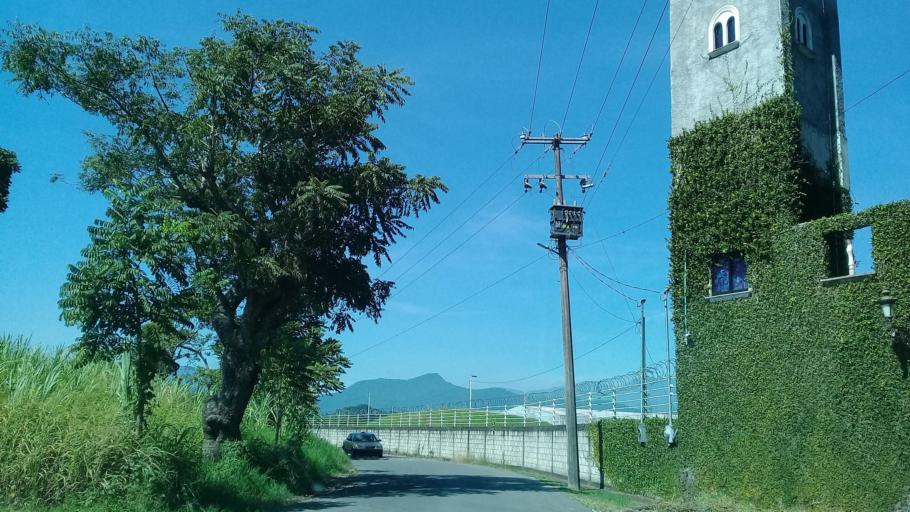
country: MX
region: Veracruz
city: Amatlan de los Reyes
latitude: 18.8550
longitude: -96.9082
